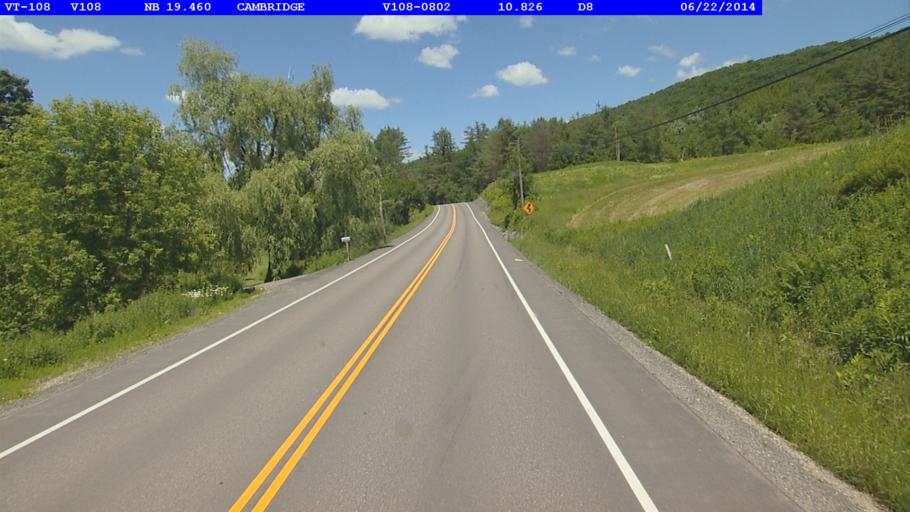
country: US
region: Vermont
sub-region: Lamoille County
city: Johnson
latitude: 44.6715
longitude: -72.8267
